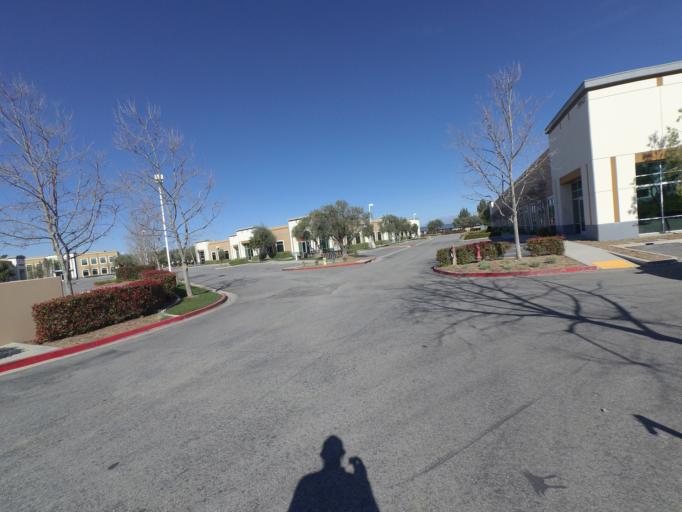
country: US
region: California
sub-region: Riverside County
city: March Air Force Base
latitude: 33.9094
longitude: -117.2852
